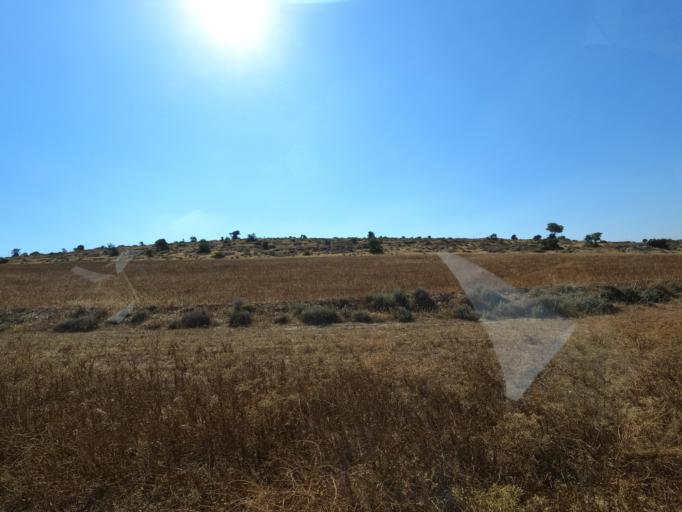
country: CY
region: Larnaka
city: Psevdas
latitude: 34.9668
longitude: 33.4777
